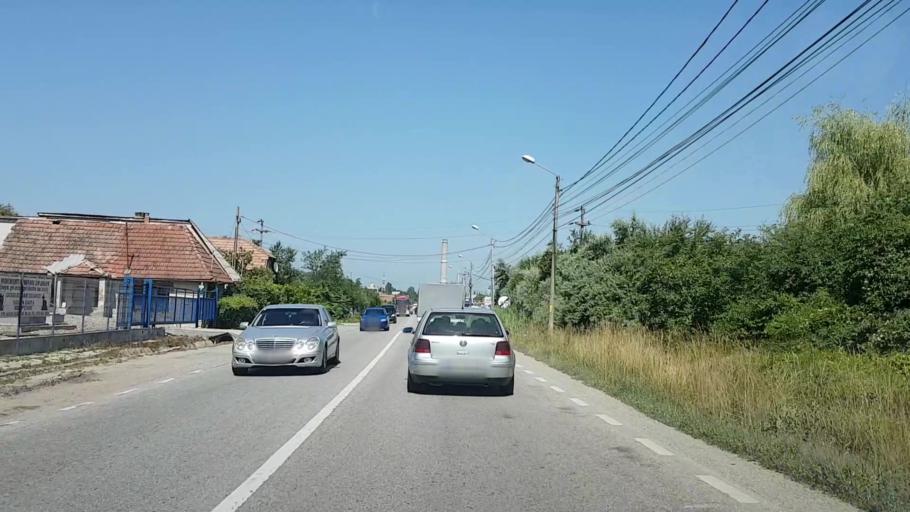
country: RO
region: Cluj
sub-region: Municipiul Dej
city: Dej
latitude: 47.1562
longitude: 23.8825
